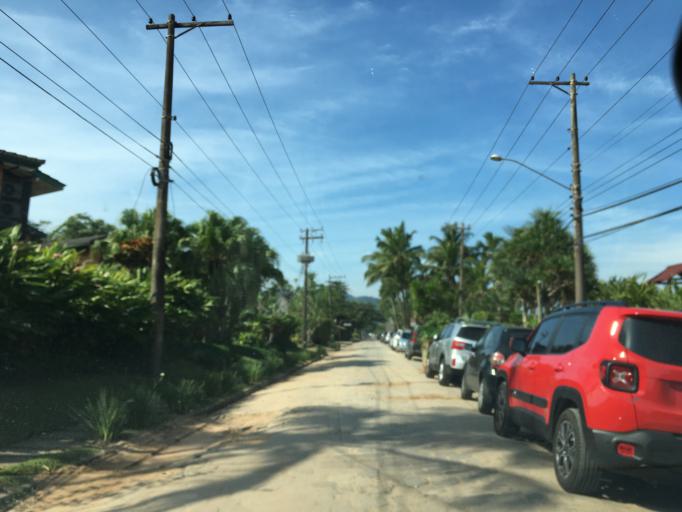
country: BR
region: Sao Paulo
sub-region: Sao Sebastiao
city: Sao Sebastiao
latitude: -23.7669
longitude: -45.7426
